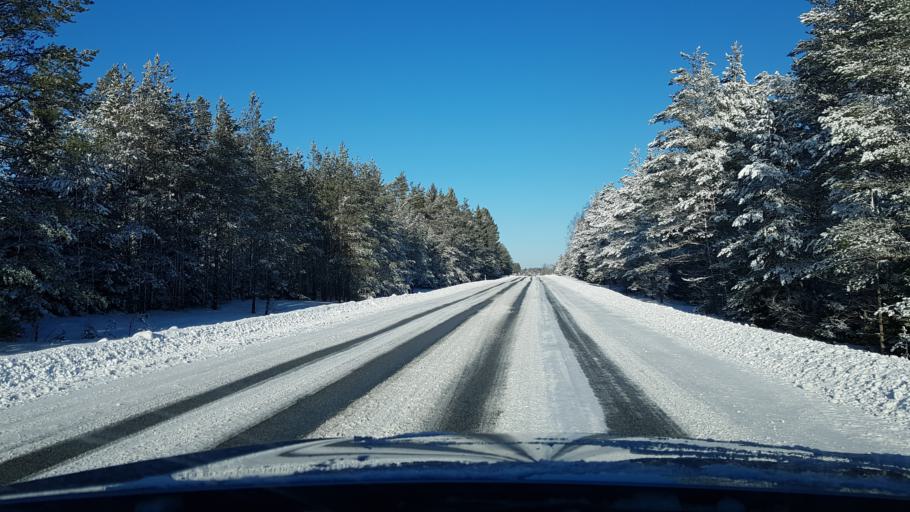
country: EE
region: Hiiumaa
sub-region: Kaerdla linn
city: Kardla
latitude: 58.9491
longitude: 22.7717
